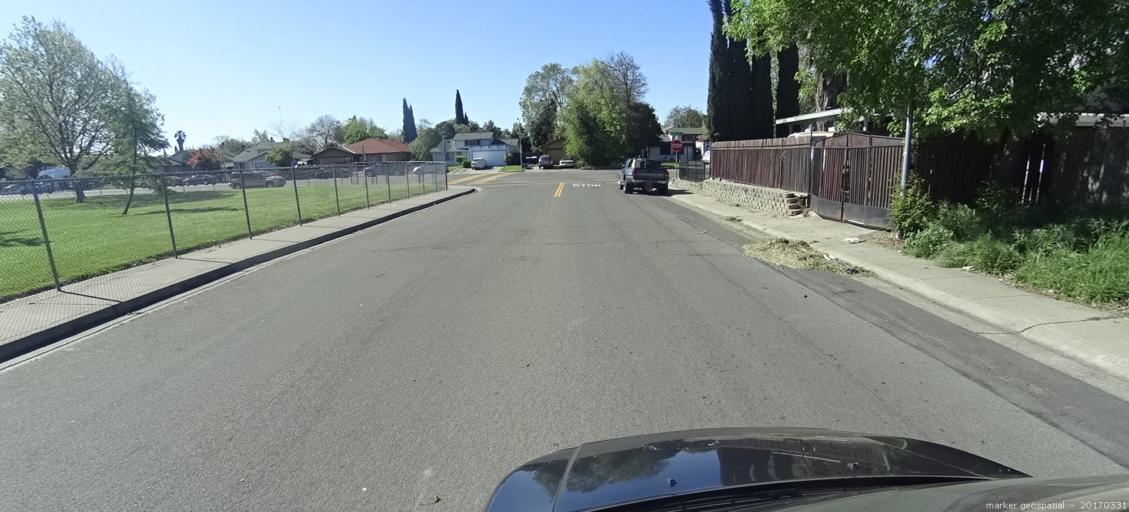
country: US
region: California
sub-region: Sacramento County
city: Parkway
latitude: 38.4669
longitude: -121.4423
